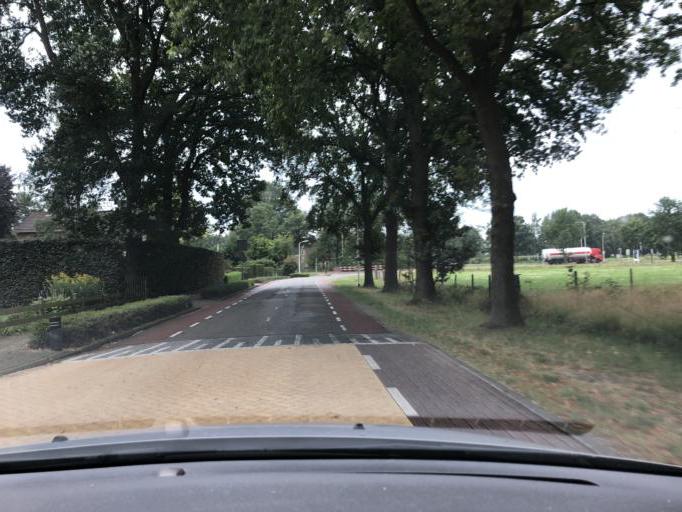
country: NL
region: Overijssel
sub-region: Gemeente Dalfsen
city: Dalfsen
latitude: 52.5328
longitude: 6.3092
